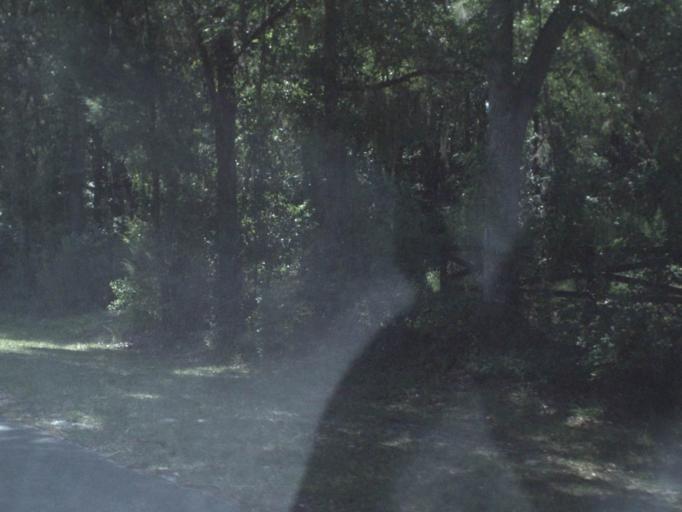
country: US
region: Florida
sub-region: Union County
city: Lake Butler
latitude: 30.0042
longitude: -82.4941
